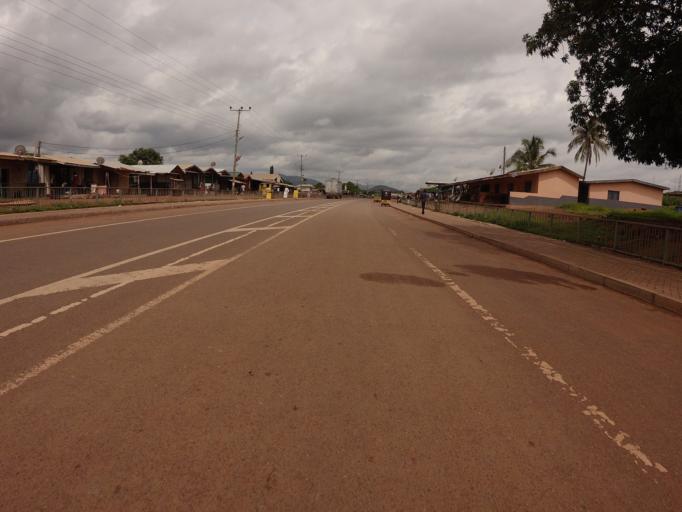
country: TG
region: Centrale
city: Sotouboua
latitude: 8.2689
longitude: 0.5188
